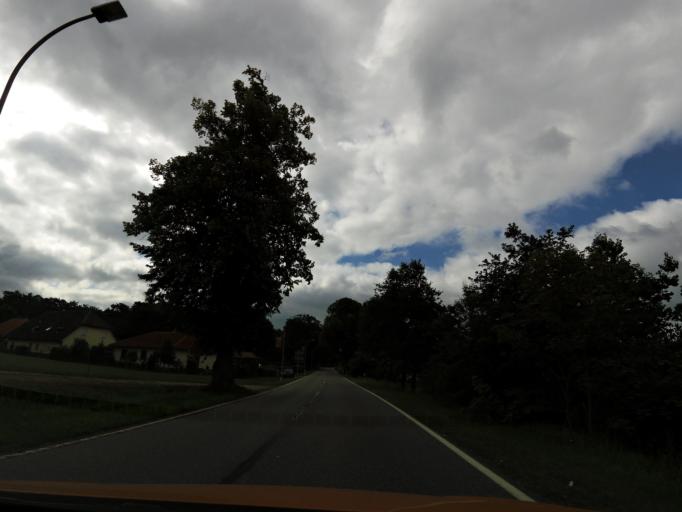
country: DE
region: Mecklenburg-Vorpommern
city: Muhl Rosin
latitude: 53.7767
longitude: 12.2423
